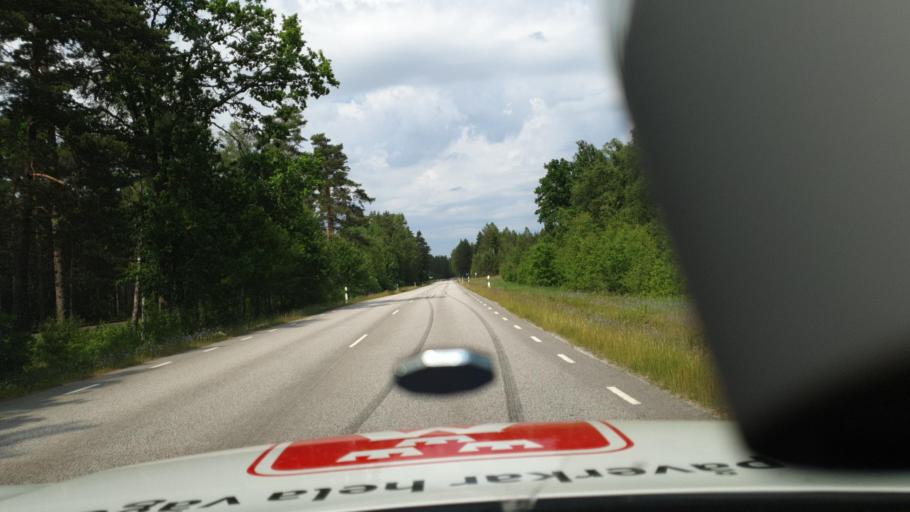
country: SE
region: Joenkoeping
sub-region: Varnamo Kommun
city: Varnamo
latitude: 57.2262
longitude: 14.0413
